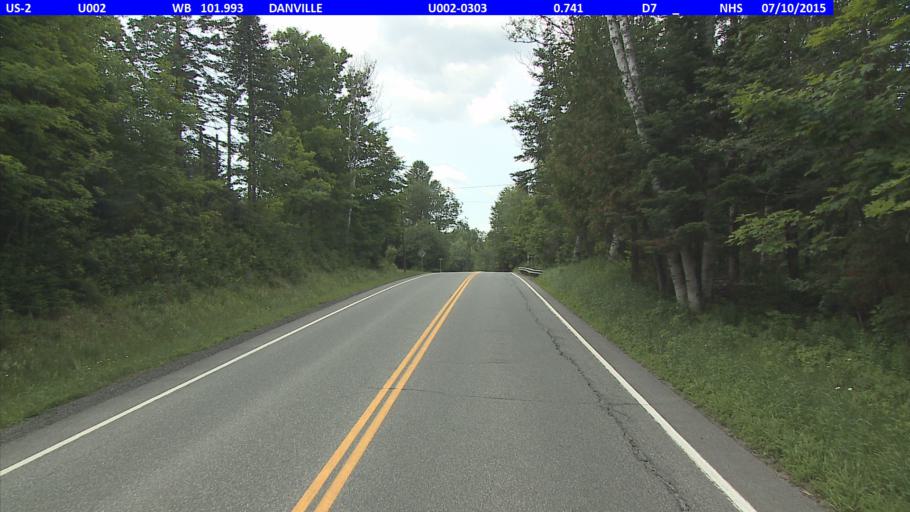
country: US
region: Vermont
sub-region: Caledonia County
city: Hardwick
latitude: 44.4060
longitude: -72.2140
